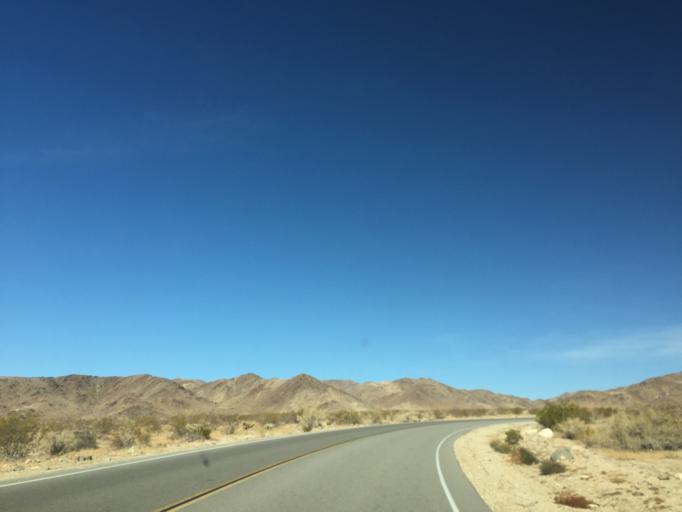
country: US
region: California
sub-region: San Bernardino County
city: Twentynine Palms
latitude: 33.9270
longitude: -115.9402
